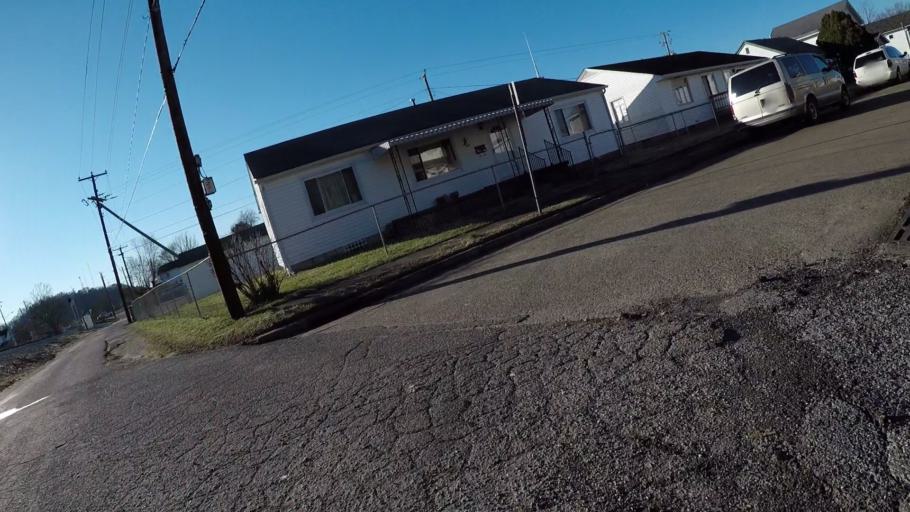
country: US
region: West Virginia
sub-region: Cabell County
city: Pea Ridge
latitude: 38.4275
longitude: -82.3811
